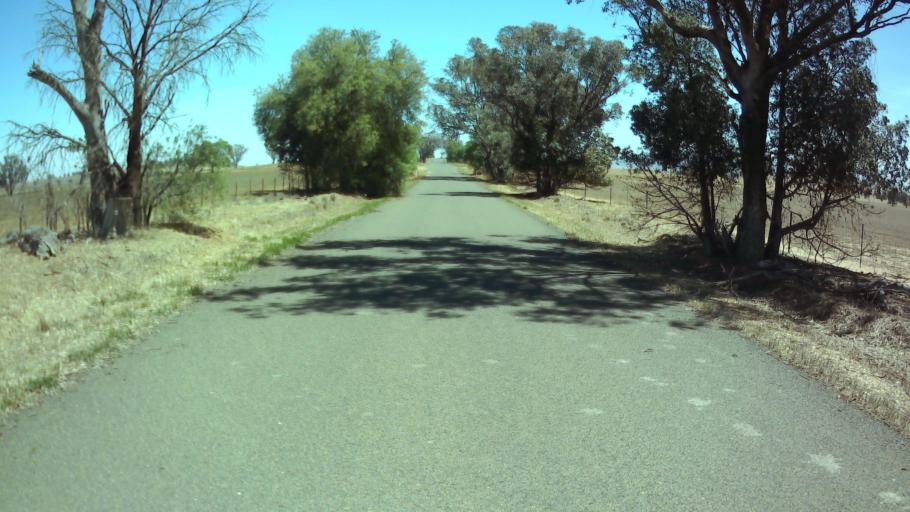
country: AU
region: New South Wales
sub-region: Weddin
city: Grenfell
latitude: -34.0551
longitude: 148.2329
